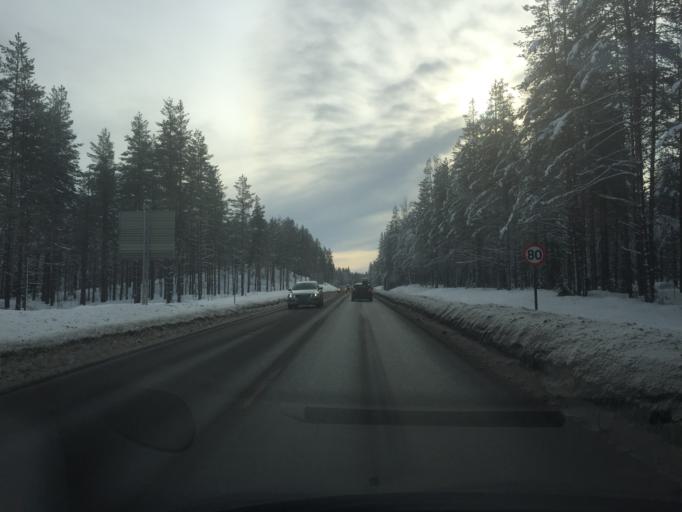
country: NO
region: Hedmark
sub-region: Trysil
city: Innbygda
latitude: 61.2927
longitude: 12.2724
